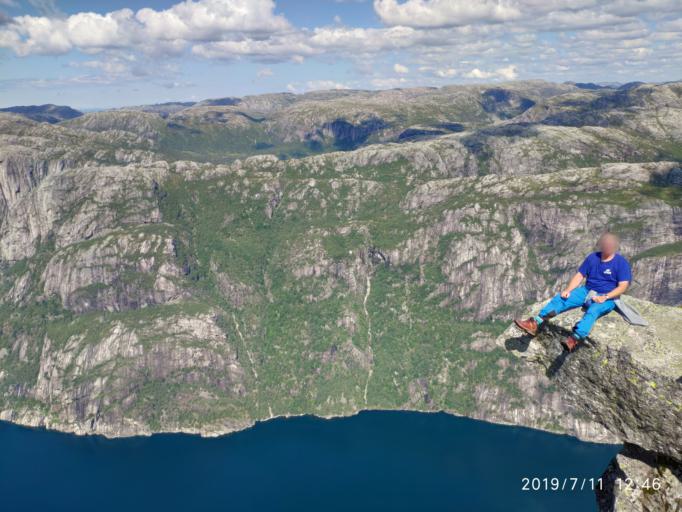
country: NO
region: Vest-Agder
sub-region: Sirdal
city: Tonstad
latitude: 59.0364
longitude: 6.5921
